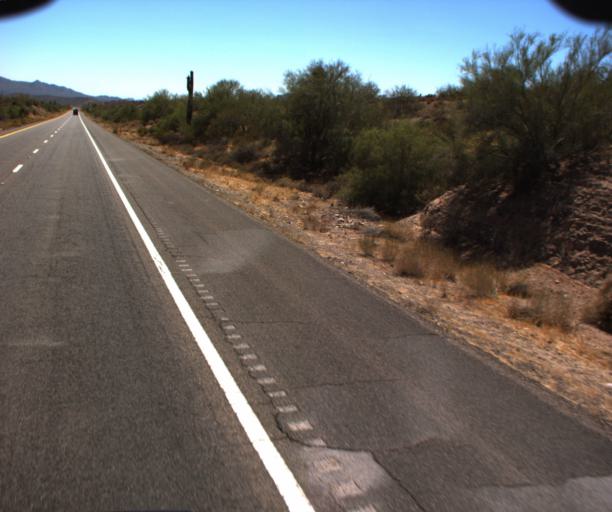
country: US
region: Arizona
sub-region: Maricopa County
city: Fountain Hills
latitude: 33.6082
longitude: -111.5819
